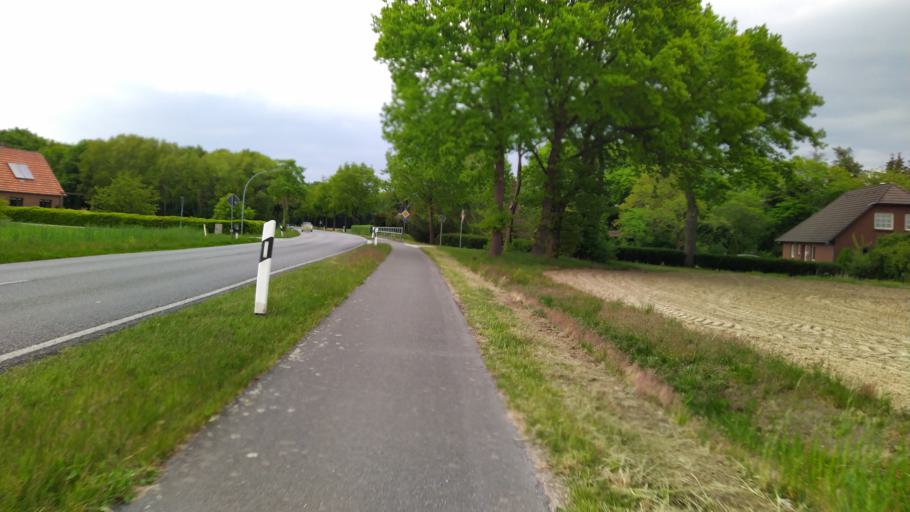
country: DE
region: Lower Saxony
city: Ostereistedt
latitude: 53.2810
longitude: 9.2169
